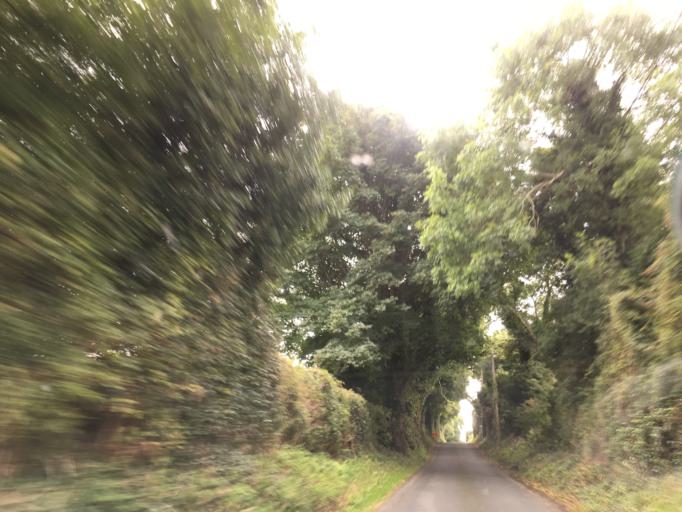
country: IE
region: Leinster
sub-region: Wicklow
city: Rathnew
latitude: 52.9209
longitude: -6.1012
